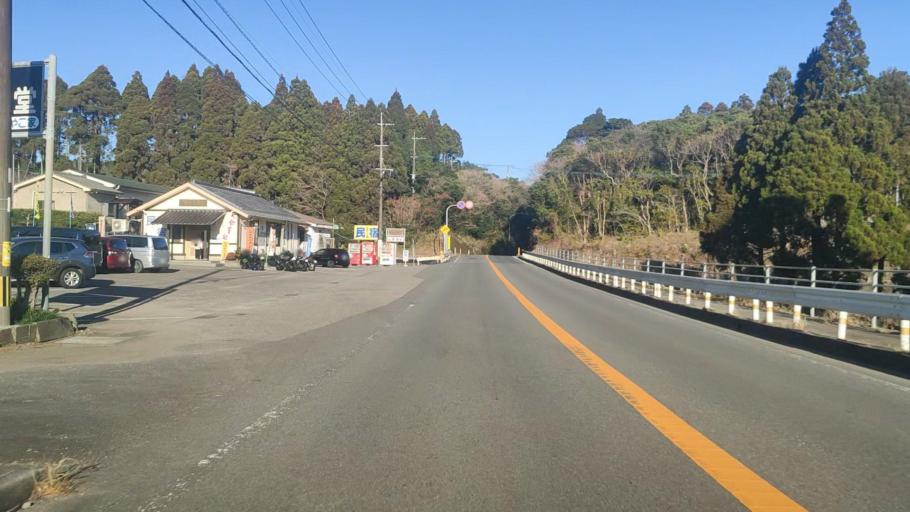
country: JP
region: Miyazaki
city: Nobeoka
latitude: 32.3460
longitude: 131.6237
